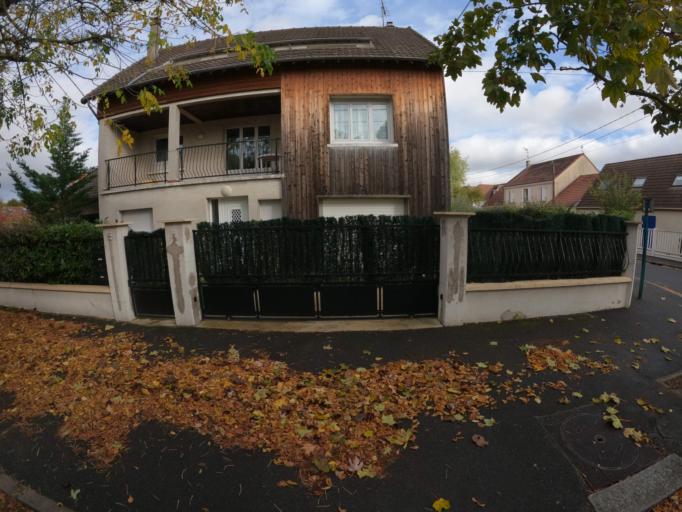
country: FR
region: Ile-de-France
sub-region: Departement de Seine-Saint-Denis
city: Coubron
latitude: 48.9116
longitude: 2.5926
